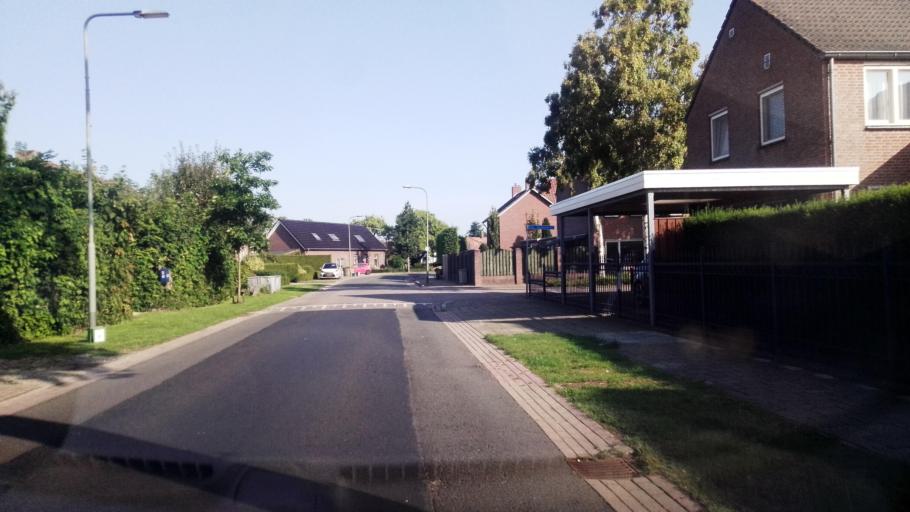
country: NL
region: Limburg
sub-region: Gemeente Bergen
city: Wellerlooi
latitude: 51.4591
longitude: 6.0849
